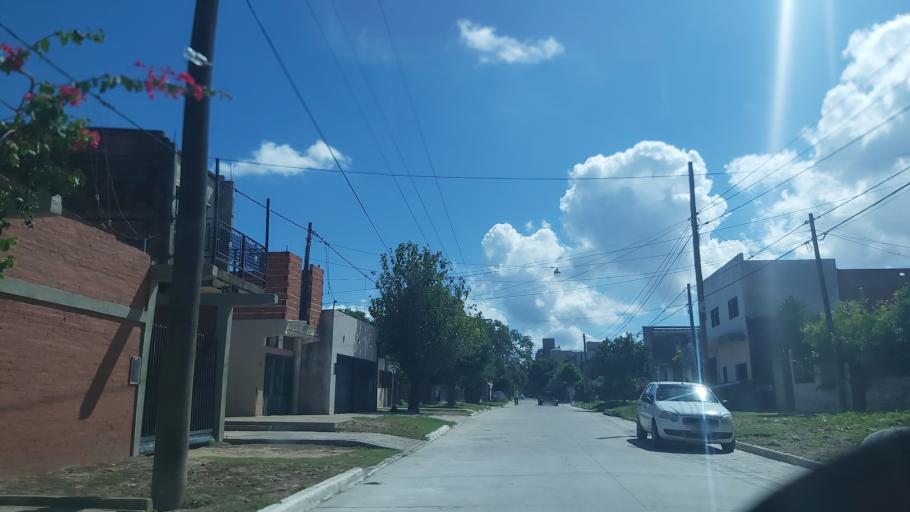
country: AR
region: Corrientes
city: Corrientes
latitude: -27.4786
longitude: -58.8501
